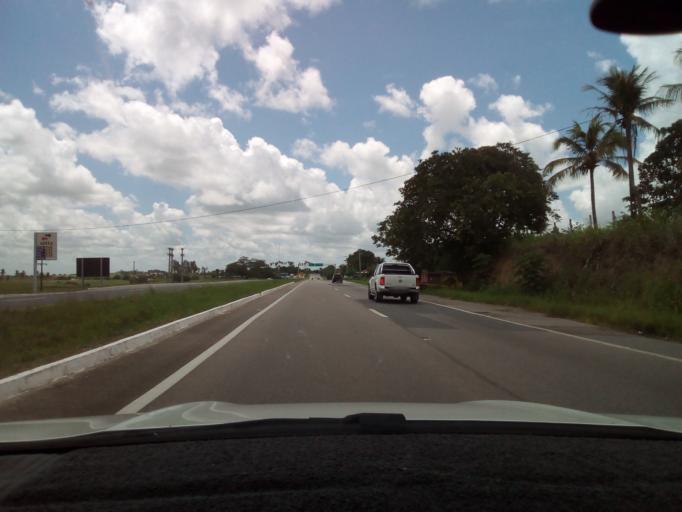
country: BR
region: Paraiba
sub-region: Pilar
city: Pilar
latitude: -7.1916
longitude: -35.2315
